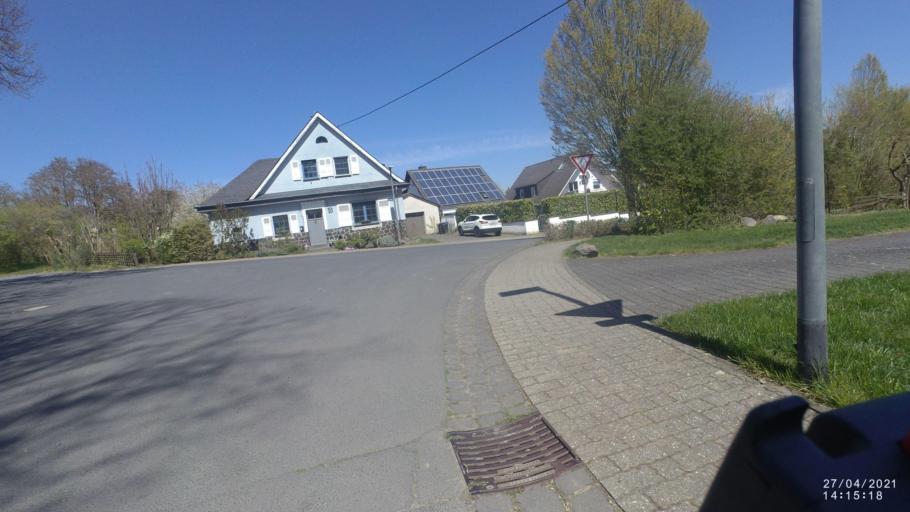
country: DE
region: Rheinland-Pfalz
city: Mertloch
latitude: 50.2705
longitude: 7.3001
